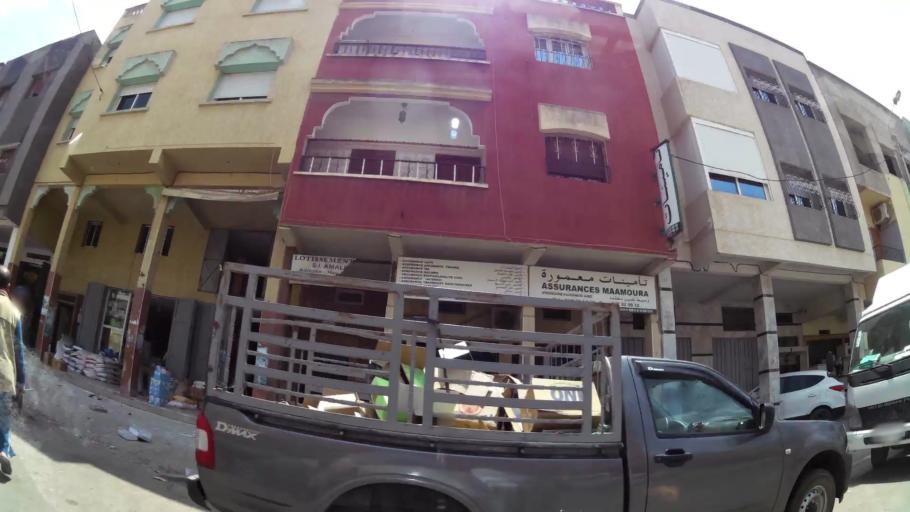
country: MA
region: Rabat-Sale-Zemmour-Zaer
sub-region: Khemisset
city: Tiflet
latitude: 34.0068
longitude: -6.5274
